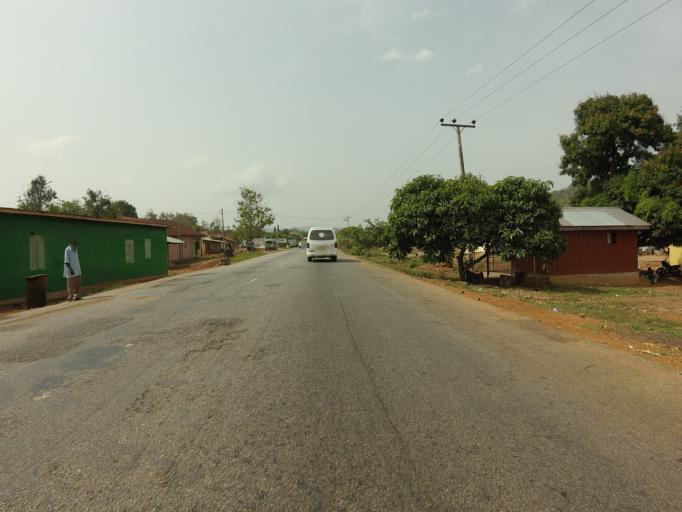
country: GH
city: Akropong
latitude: 6.3136
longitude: 0.1556
